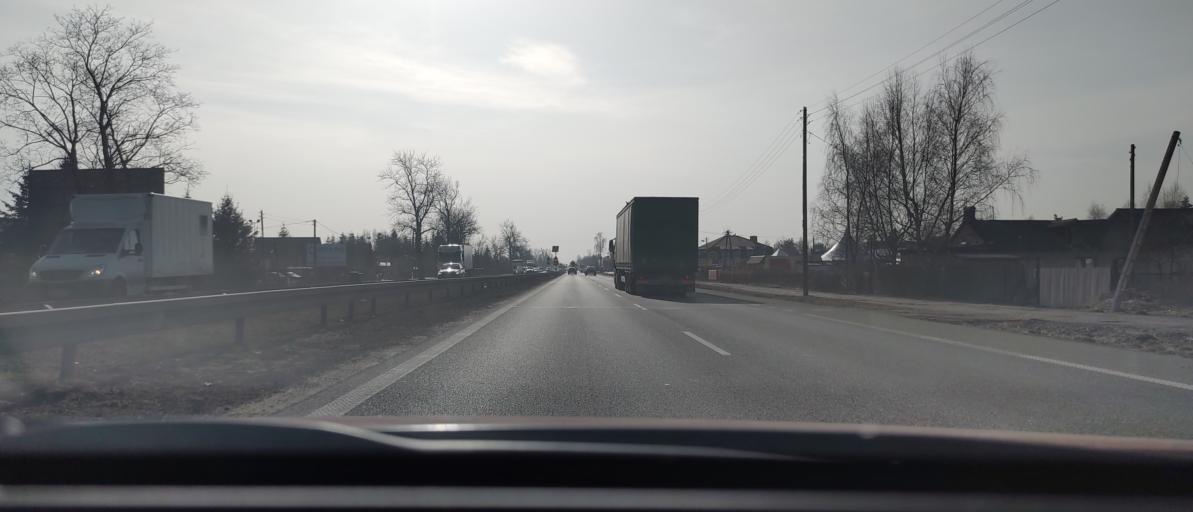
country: PL
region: Masovian Voivodeship
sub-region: Powiat pruszkowski
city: Nadarzyn
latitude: 52.0516
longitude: 20.8667
